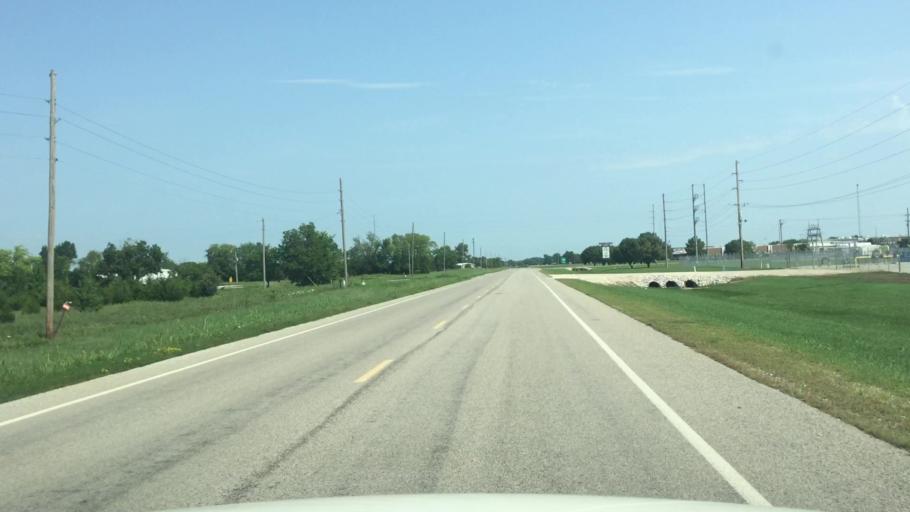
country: US
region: Kansas
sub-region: Montgomery County
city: Coffeyville
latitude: 37.0922
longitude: -95.5862
